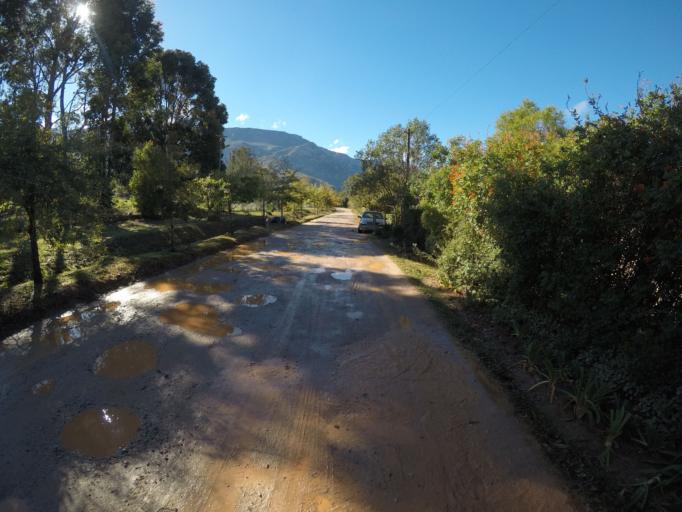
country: ZA
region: Western Cape
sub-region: Overberg District Municipality
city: Caledon
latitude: -34.0476
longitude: 19.6083
